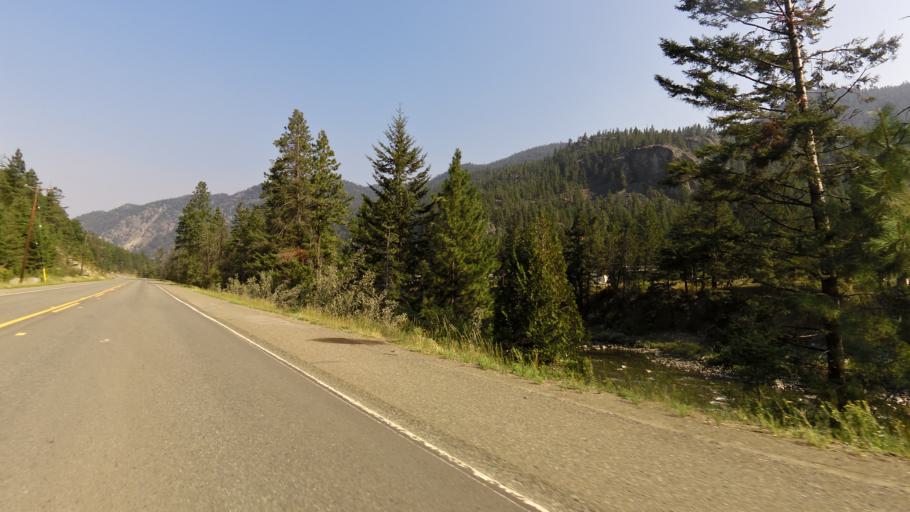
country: CA
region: British Columbia
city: Princeton
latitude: 49.3865
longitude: -120.2016
